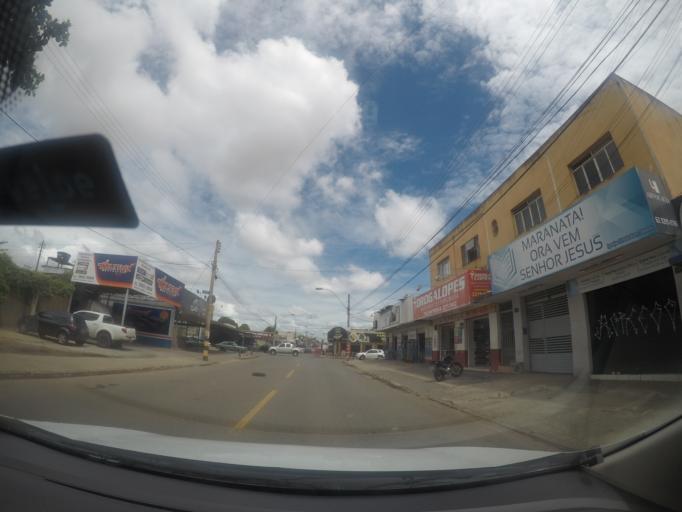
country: BR
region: Goias
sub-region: Goiania
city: Goiania
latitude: -16.6634
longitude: -49.3016
